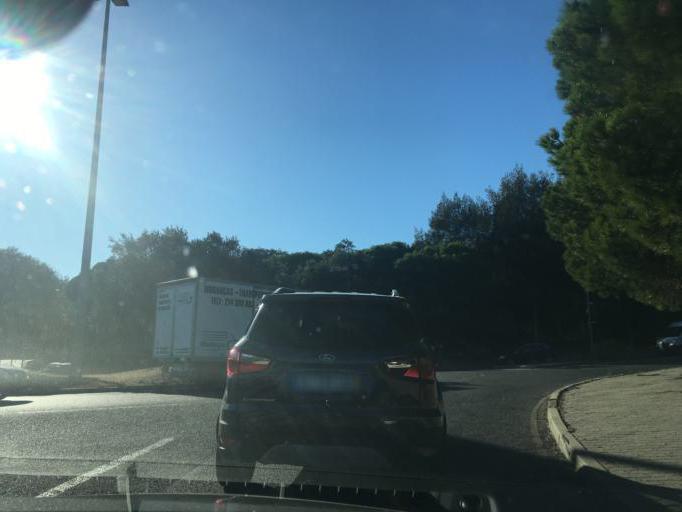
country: PT
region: Lisbon
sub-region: Oeiras
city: Alges
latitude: 38.7138
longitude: -9.2007
